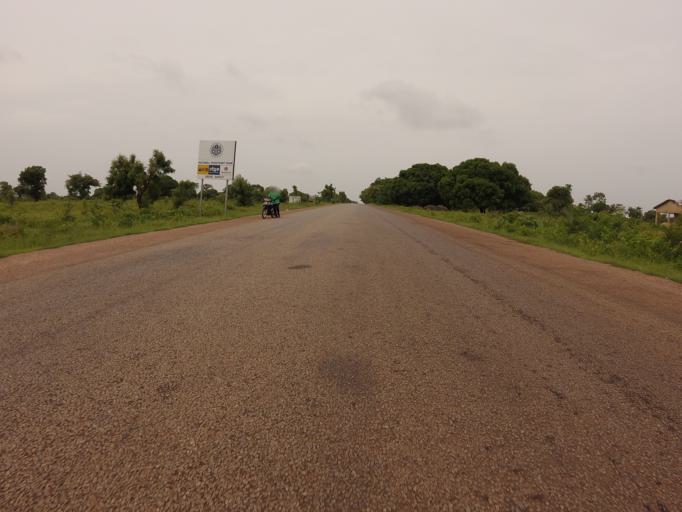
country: GH
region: Northern
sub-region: Yendi
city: Yendi
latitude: 9.4264
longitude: -0.0089
